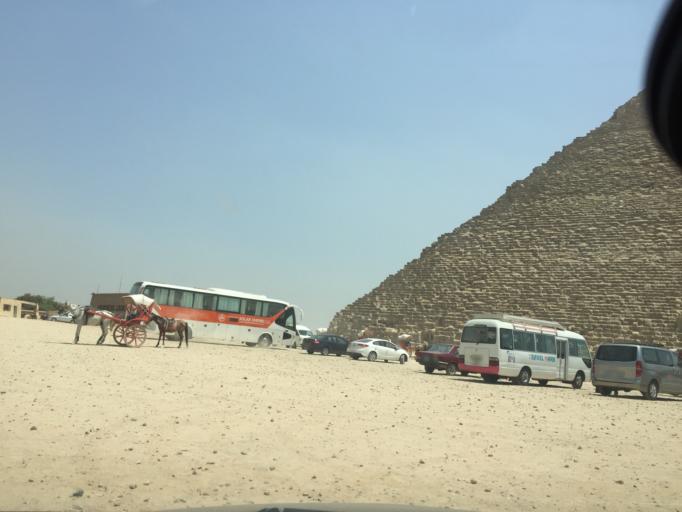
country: EG
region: Al Jizah
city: Al Jizah
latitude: 29.9813
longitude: 31.1343
